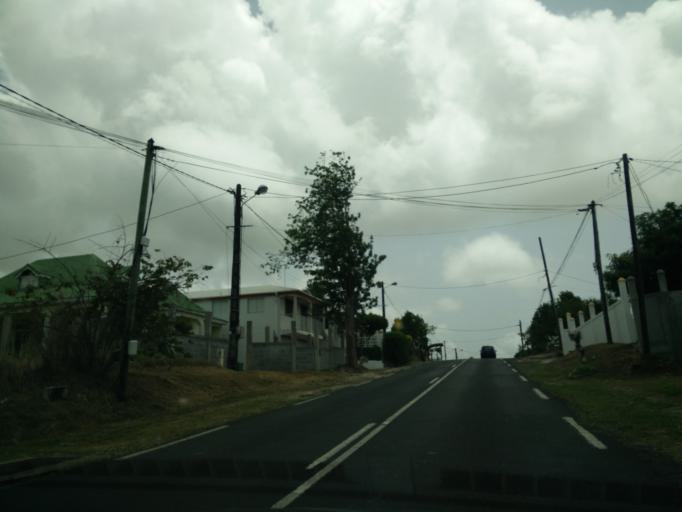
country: GP
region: Guadeloupe
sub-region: Guadeloupe
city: Petit-Canal
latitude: 16.3595
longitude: -61.4557
